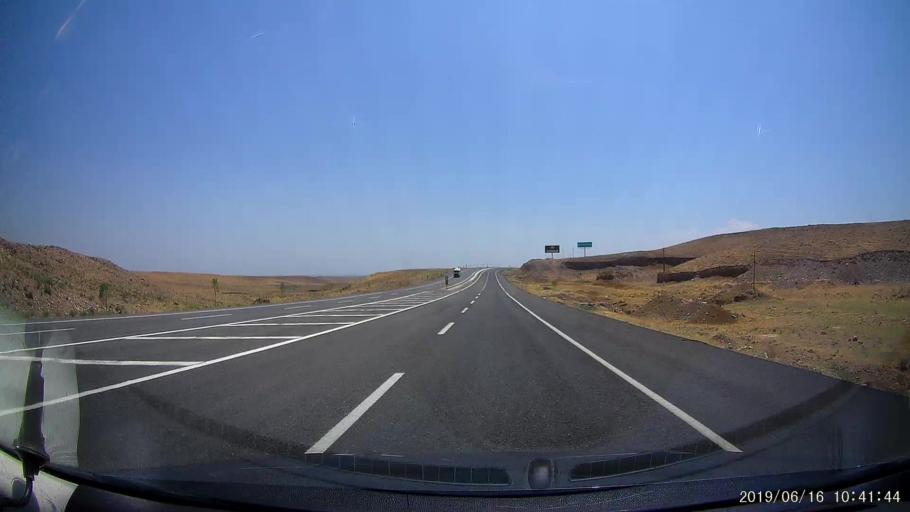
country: TR
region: Igdir
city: Tuzluca
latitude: 40.0463
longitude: 43.7904
